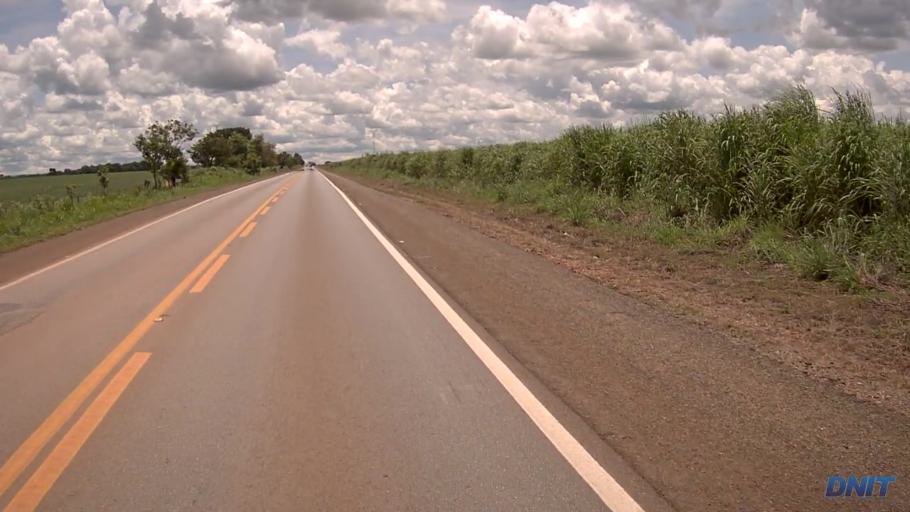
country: BR
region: Goias
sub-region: Uruacu
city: Uruacu
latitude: -14.7153
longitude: -49.0879
